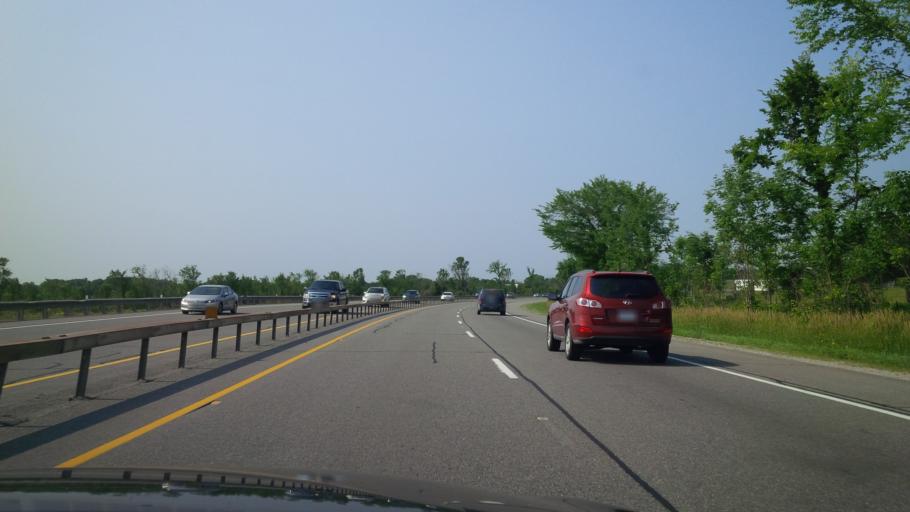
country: CA
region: Ontario
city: Orillia
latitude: 44.5117
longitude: -79.4702
